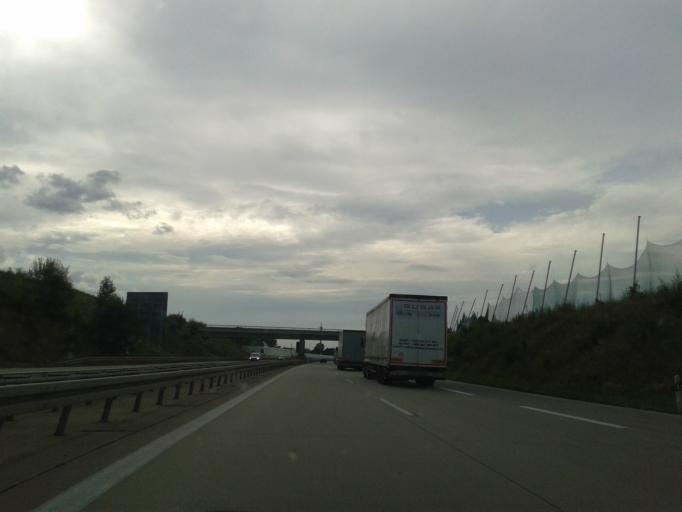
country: DE
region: Saxony
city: Kreischa
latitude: 50.9769
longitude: 13.8038
